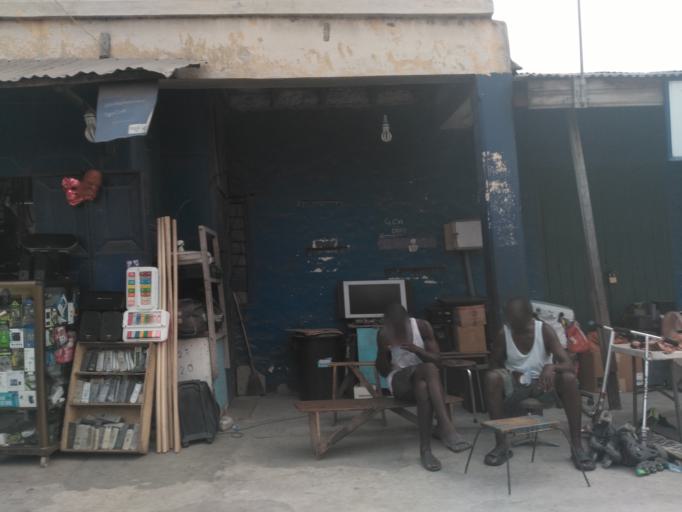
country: GH
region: Greater Accra
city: Accra
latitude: 5.5387
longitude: -0.2146
